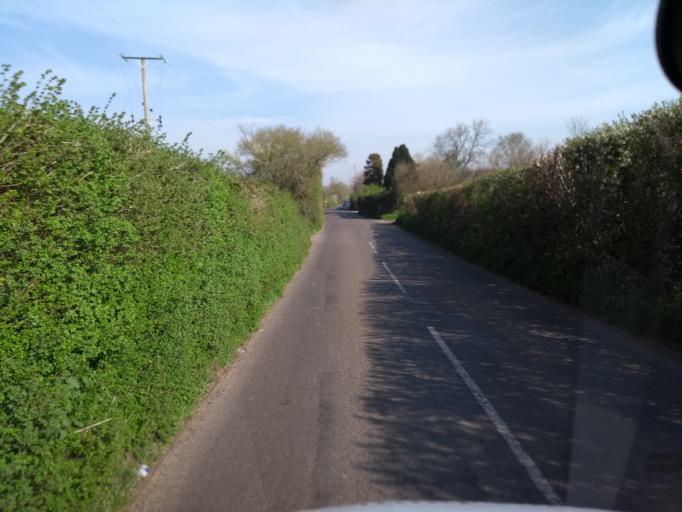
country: GB
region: England
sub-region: Somerset
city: Creech Saint Michael
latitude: 51.0159
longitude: -3.0427
